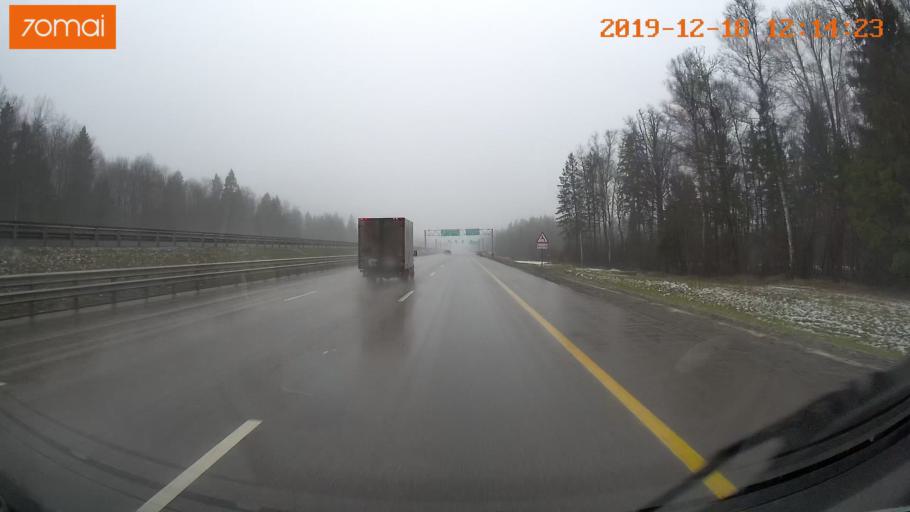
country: RU
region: Moskovskaya
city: Rumyantsevo
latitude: 55.9597
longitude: 36.5095
